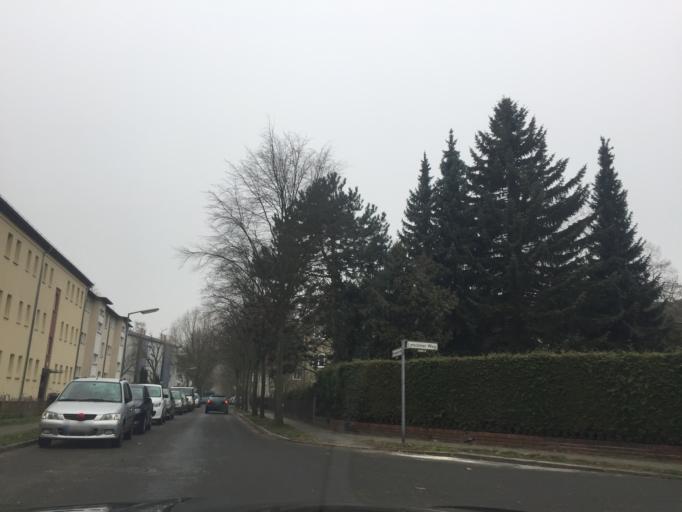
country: DE
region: Berlin
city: Tegel
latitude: 52.5856
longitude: 13.2988
